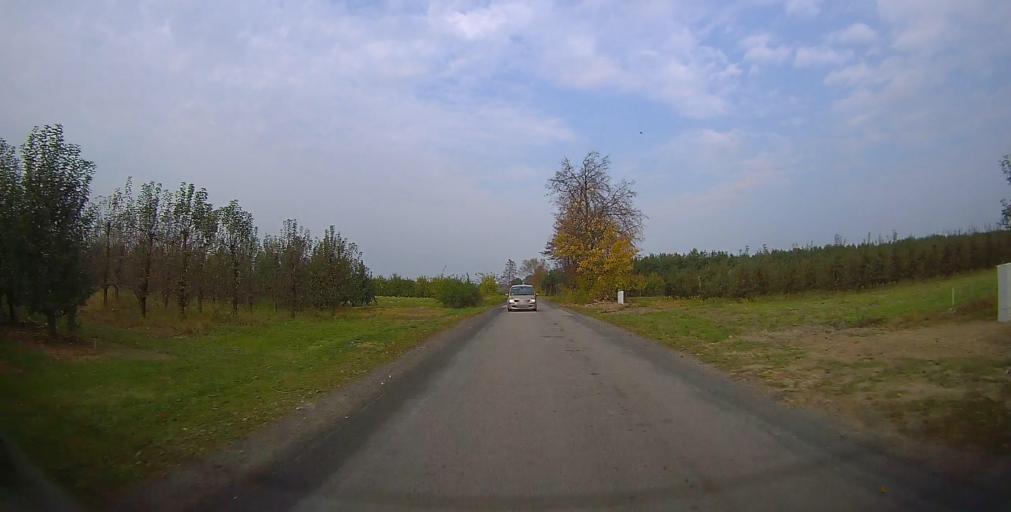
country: PL
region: Masovian Voivodeship
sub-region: Powiat grojecki
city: Mogielnica
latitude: 51.6526
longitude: 20.7239
